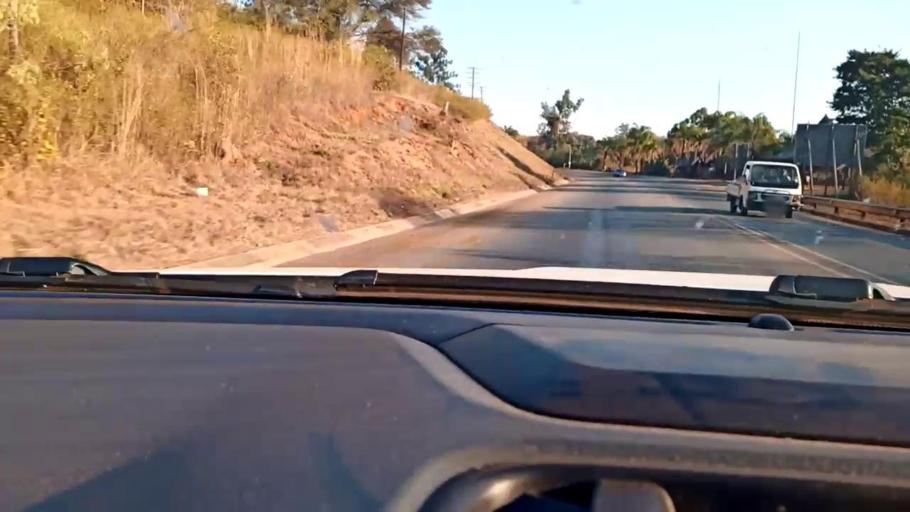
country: ZA
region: Limpopo
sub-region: Mopani District Municipality
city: Duiwelskloof
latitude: -23.6889
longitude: 30.1471
